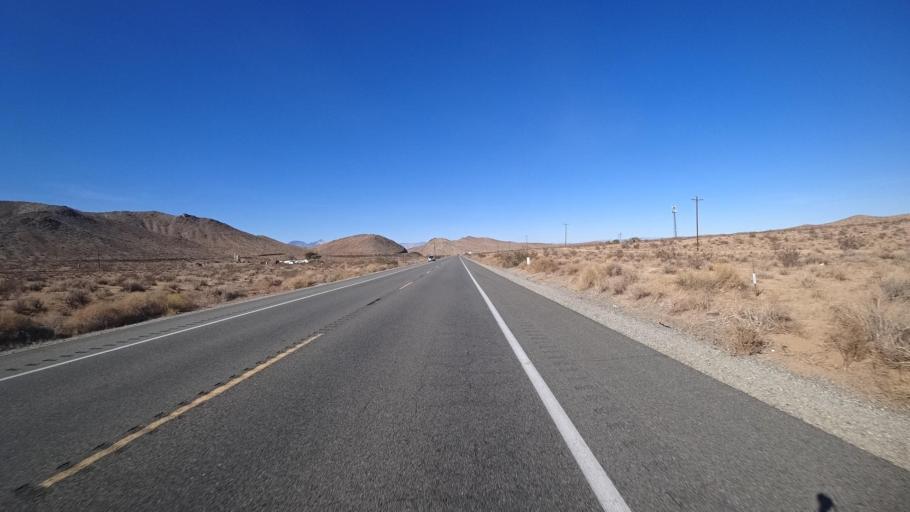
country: US
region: California
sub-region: Kern County
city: Ridgecrest
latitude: 35.5368
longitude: -117.6858
